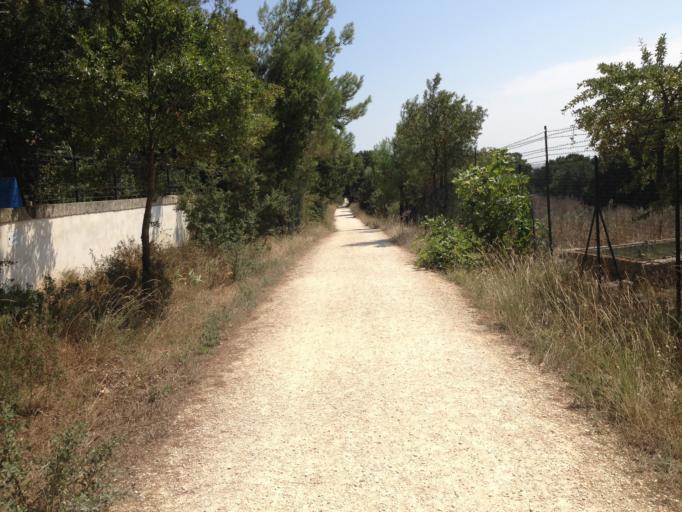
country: IT
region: Apulia
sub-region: Provincia di Brindisi
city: Cisternino
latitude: 40.7135
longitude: 17.4079
